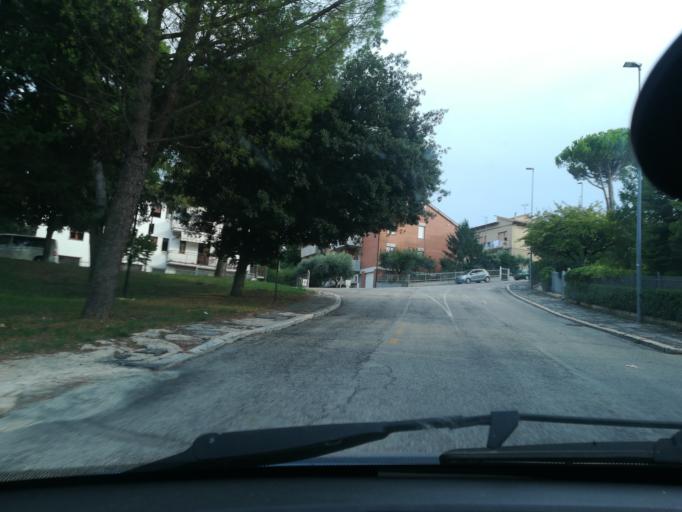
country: IT
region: The Marches
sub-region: Provincia di Macerata
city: Macerata
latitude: 43.3084
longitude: 13.4628
